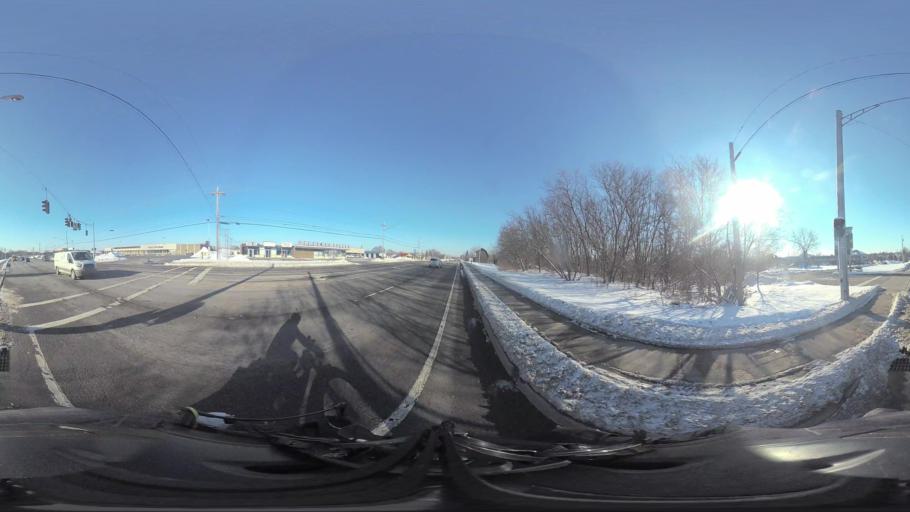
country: US
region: New York
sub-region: Monroe County
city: Rochester
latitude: 43.0699
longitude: -77.6075
